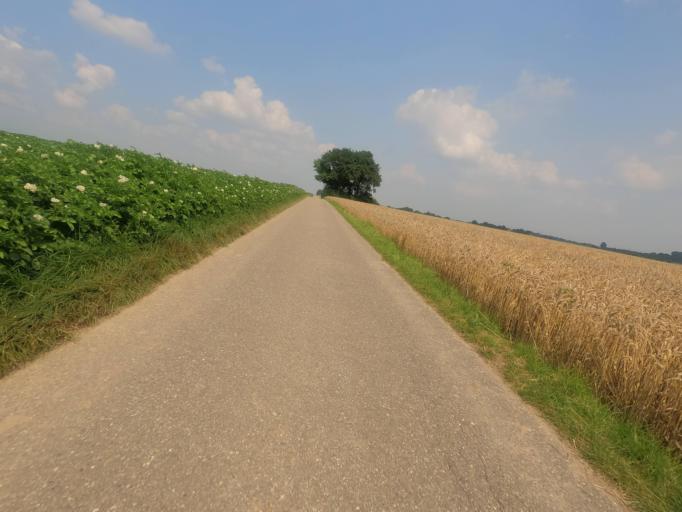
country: DE
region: North Rhine-Westphalia
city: Baesweiler
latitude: 50.9342
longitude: 6.1674
